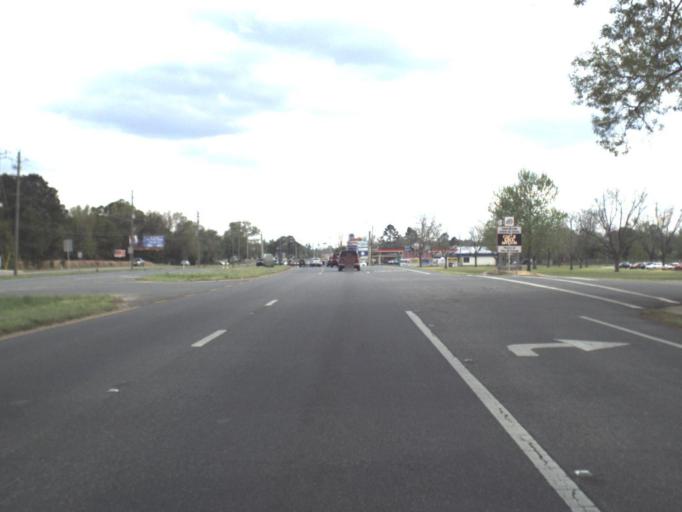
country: US
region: Florida
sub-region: Okaloosa County
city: Crestview
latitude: 30.7903
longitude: -86.5586
